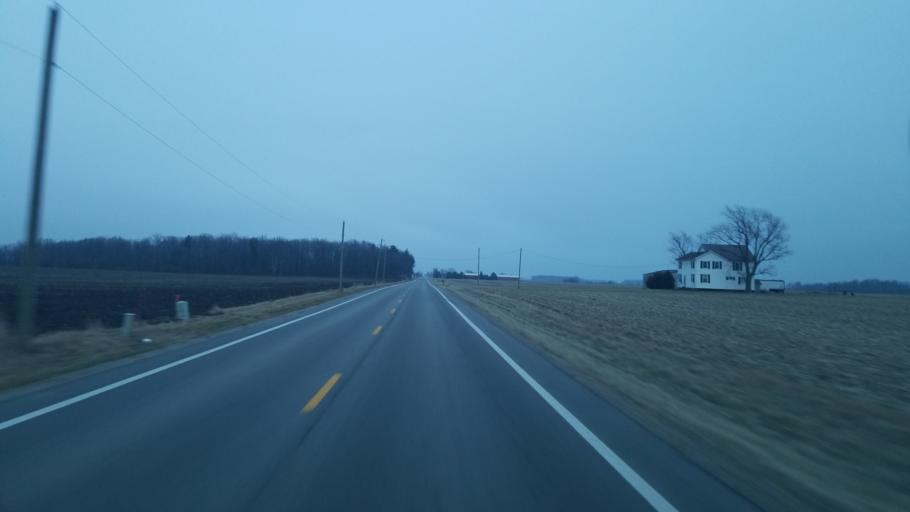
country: US
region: Ohio
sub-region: Mercer County
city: Rockford
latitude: 40.6548
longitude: -84.7064
